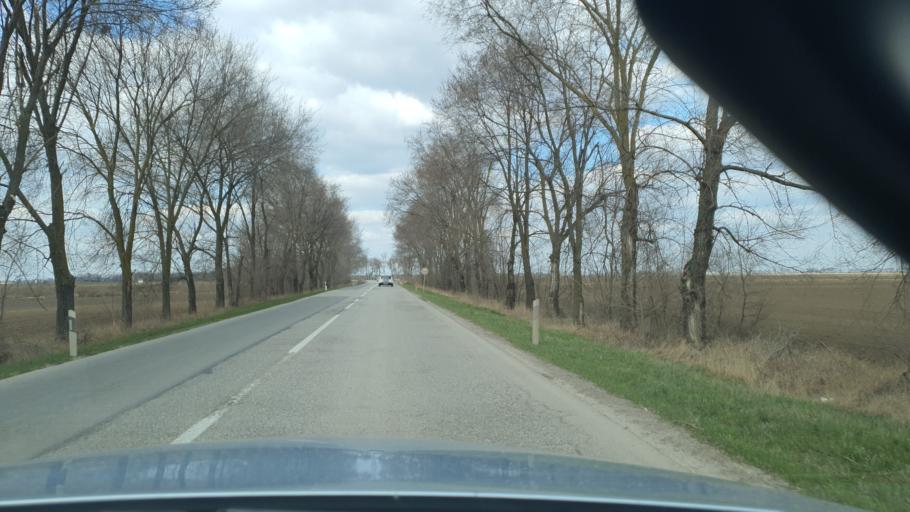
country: RS
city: Obrovac
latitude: 45.4402
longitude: 19.3713
